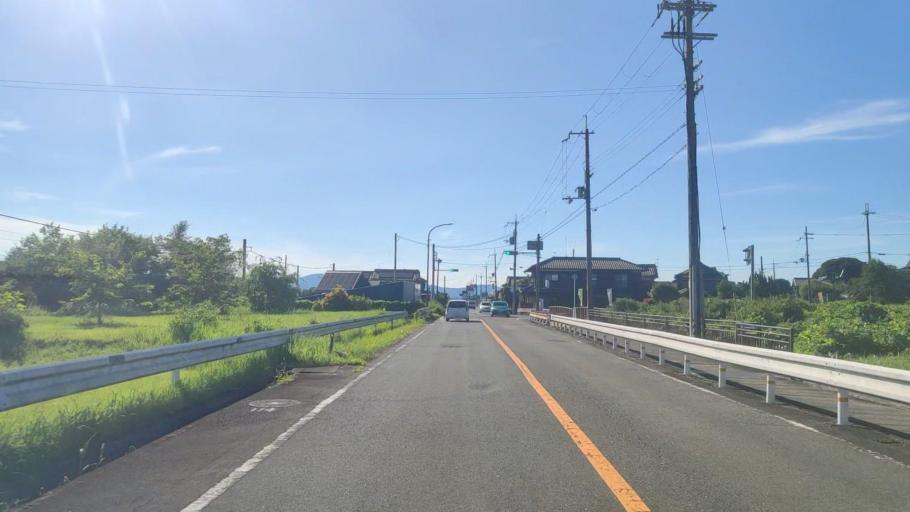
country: JP
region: Shiga Prefecture
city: Minakuchicho-matoba
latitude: 34.8926
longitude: 136.2264
